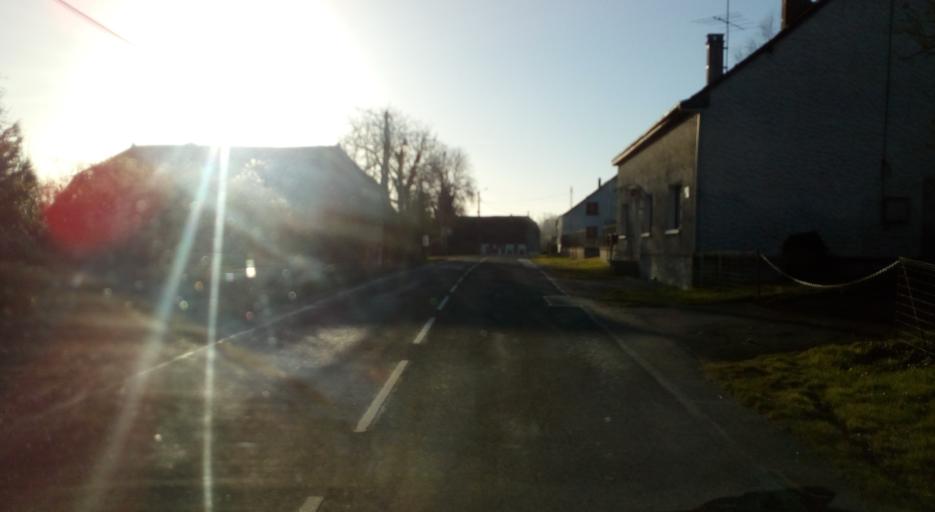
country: FR
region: Champagne-Ardenne
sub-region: Departement des Ardennes
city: Signy-le-Petit
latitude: 49.7563
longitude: 4.3177
